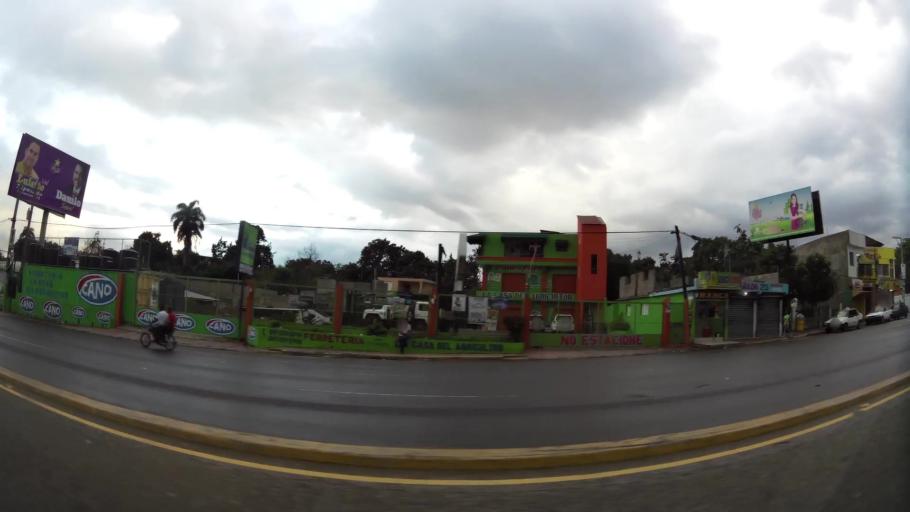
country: DO
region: Santo Domingo
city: Santo Domingo Oeste
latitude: 18.5685
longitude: -70.0922
